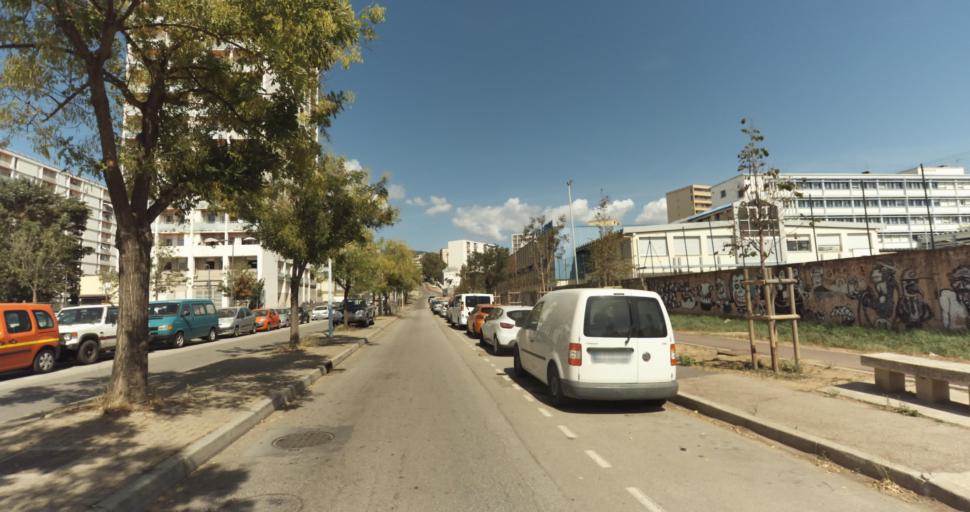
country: FR
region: Corsica
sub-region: Departement de la Corse-du-Sud
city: Ajaccio
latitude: 41.9362
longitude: 8.7509
